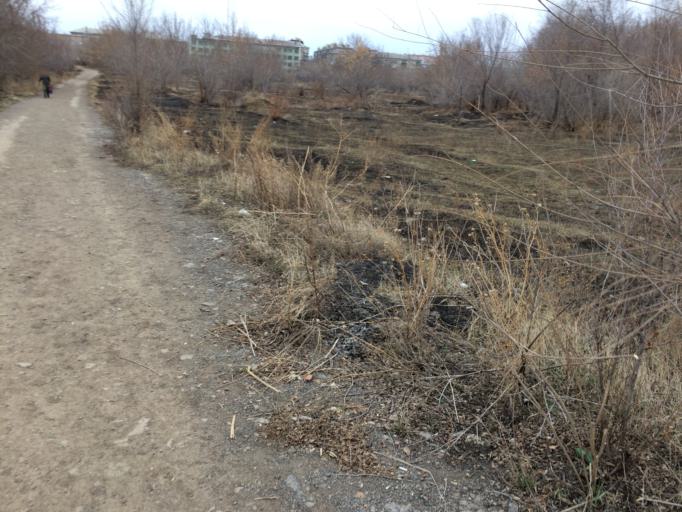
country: RU
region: Chelyabinsk
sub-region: Gorod Magnitogorsk
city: Magnitogorsk
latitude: 53.4409
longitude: 58.9767
